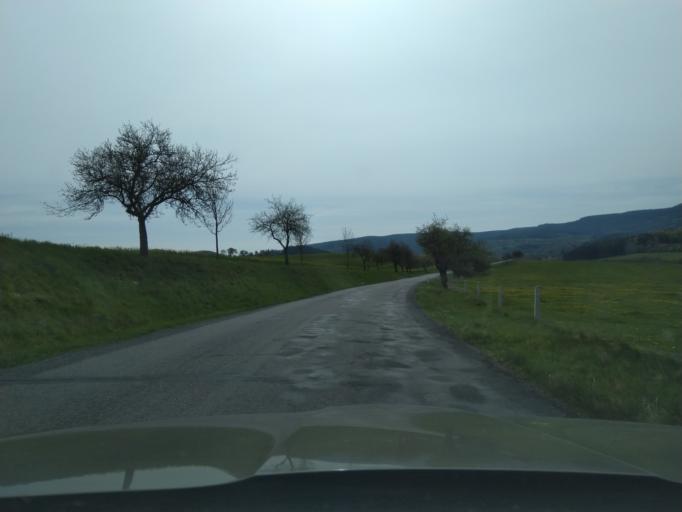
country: CZ
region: Plzensky
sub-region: Okres Klatovy
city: Kasperske Hory
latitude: 49.2010
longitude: 13.6147
